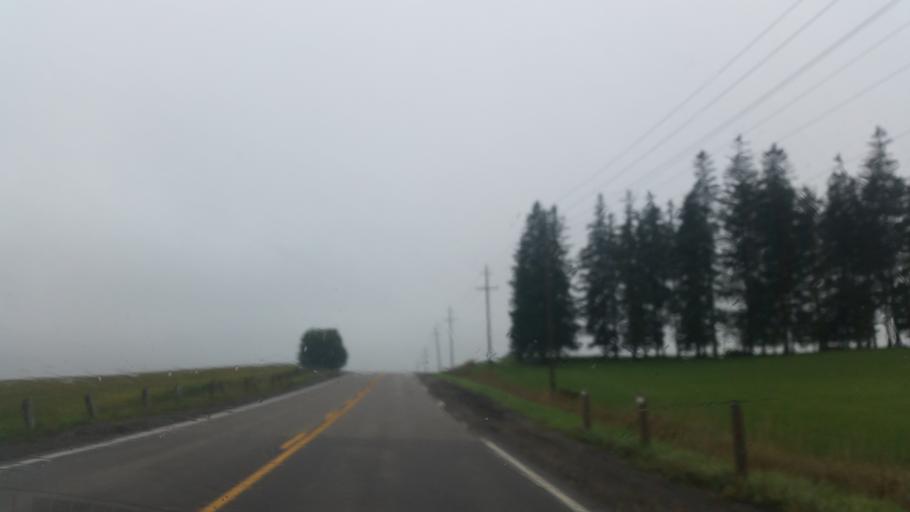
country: CA
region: Ontario
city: Waterloo
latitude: 43.6828
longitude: -80.4603
